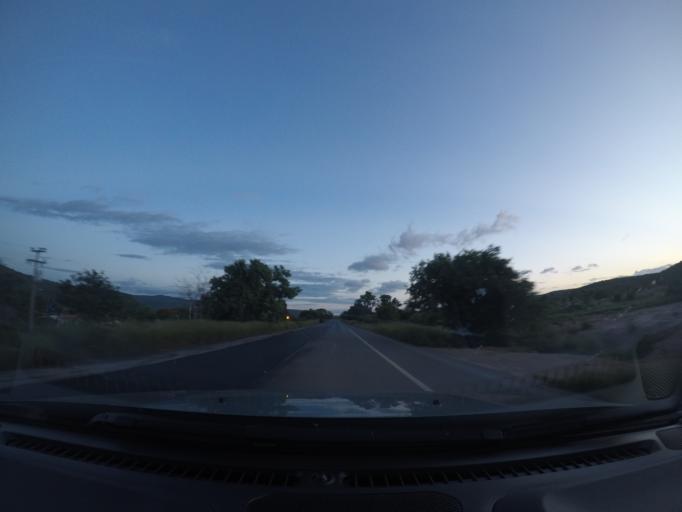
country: BR
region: Bahia
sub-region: Seabra
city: Seabra
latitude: -12.4750
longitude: -41.7409
